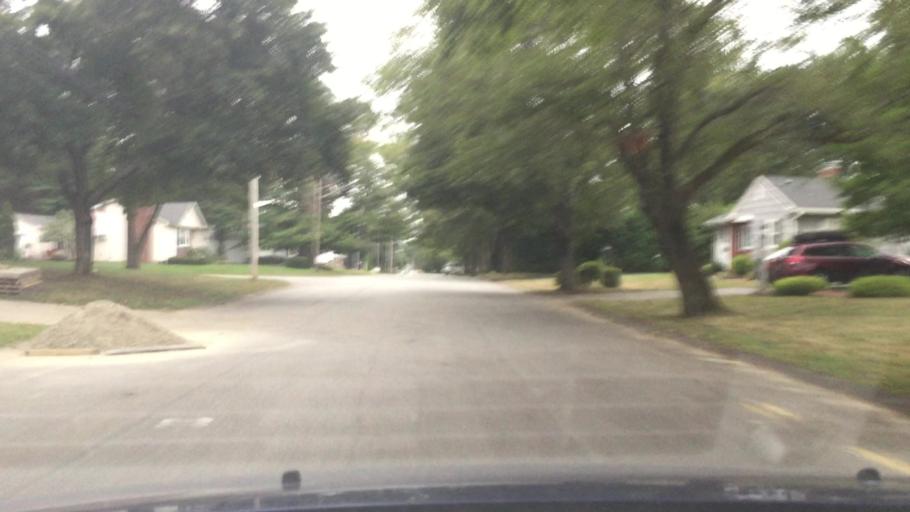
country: US
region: Massachusetts
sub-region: Essex County
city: North Andover
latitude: 42.6957
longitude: -71.1292
